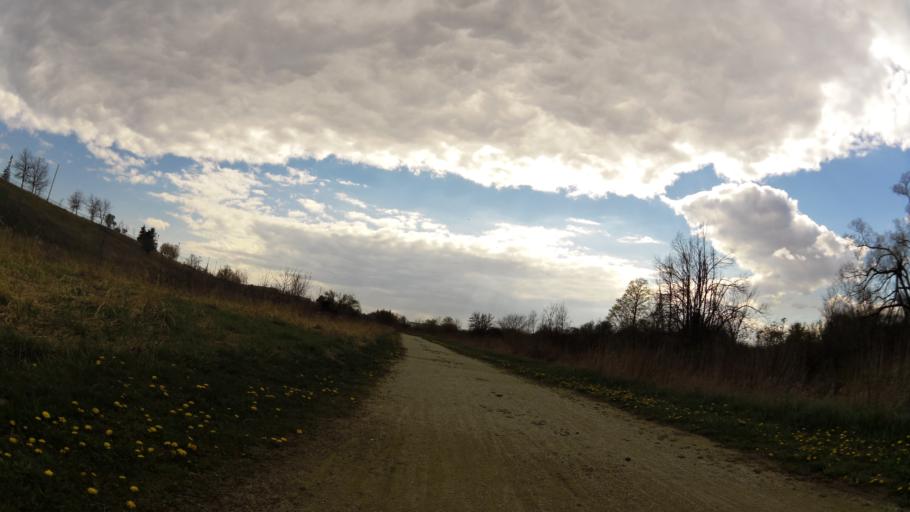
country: CA
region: Ontario
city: Etobicoke
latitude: 43.6706
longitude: -79.6543
